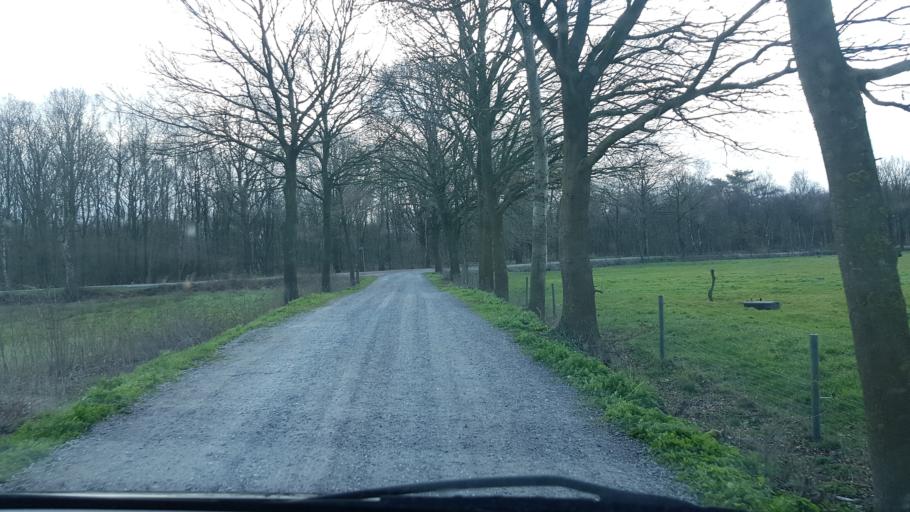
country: DE
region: Lower Saxony
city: Westerstede
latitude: 53.1709
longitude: 7.9015
